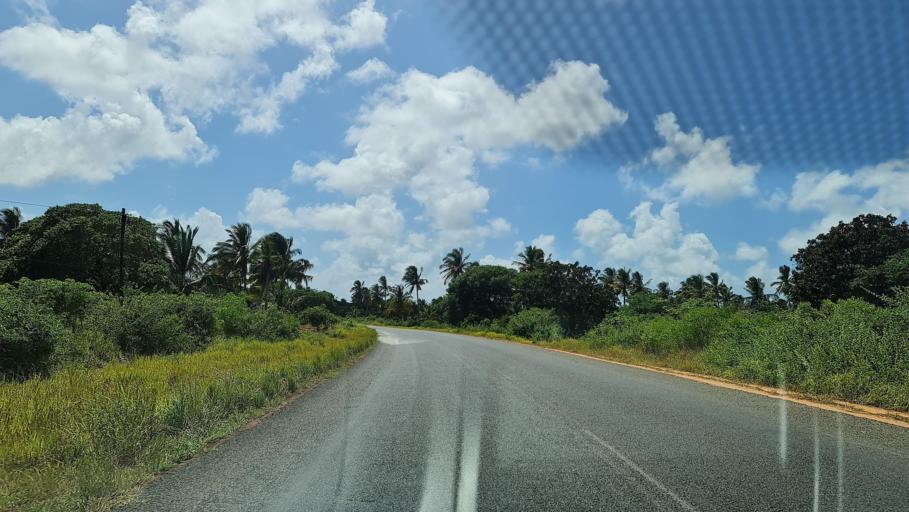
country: MZ
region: Inhambane
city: Maxixe
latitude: -24.5399
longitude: 34.9327
